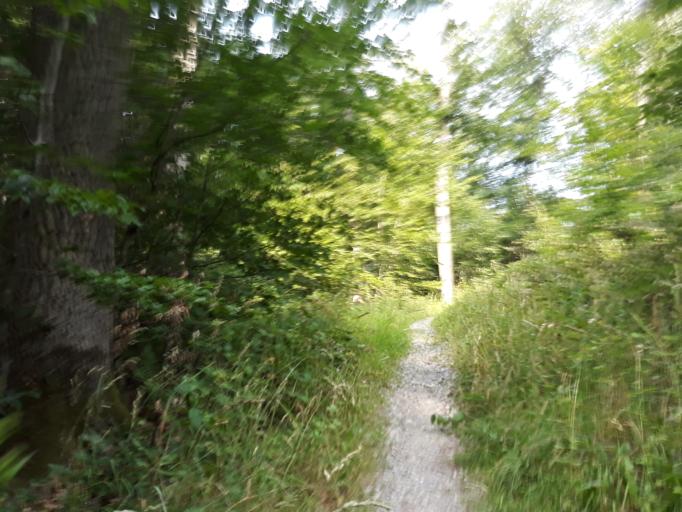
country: DE
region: Baden-Wuerttemberg
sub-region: Regierungsbezirk Stuttgart
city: Sindelfingen
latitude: 48.6921
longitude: 9.0352
